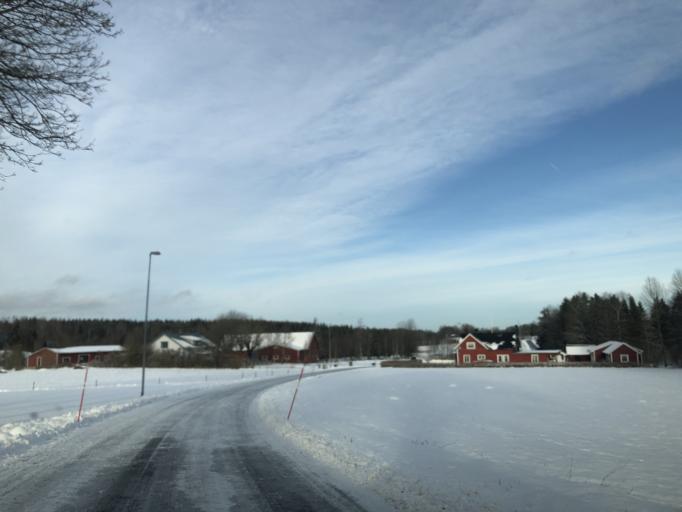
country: SE
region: Vaestra Goetaland
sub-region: Ulricehamns Kommun
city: Ulricehamn
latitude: 57.7878
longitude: 13.5264
